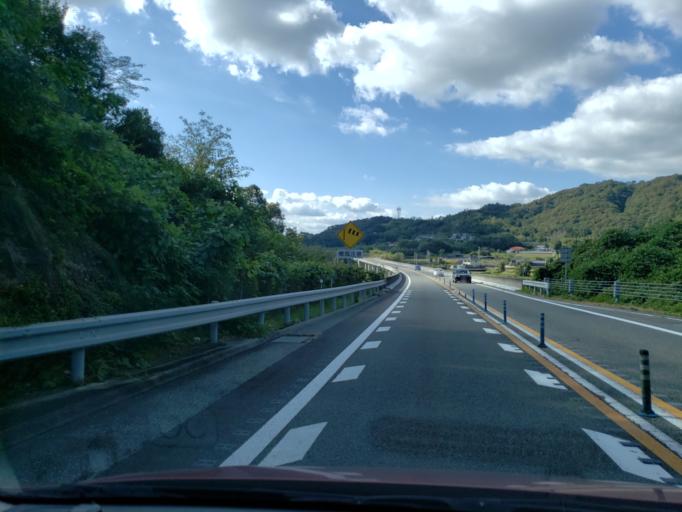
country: JP
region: Tokushima
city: Ishii
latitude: 34.1361
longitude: 134.3975
